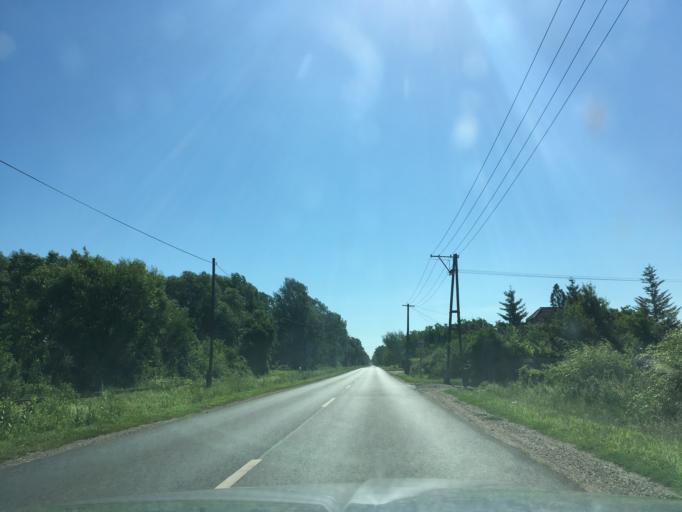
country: HU
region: Hajdu-Bihar
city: Debrecen
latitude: 47.5301
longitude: 21.7119
